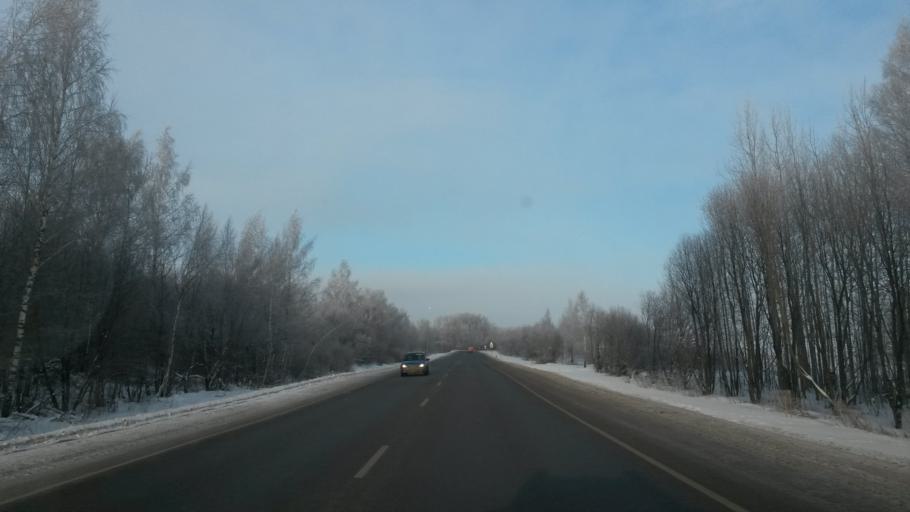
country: RU
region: Vladimir
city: Bogolyubovo
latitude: 56.2083
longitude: 40.4421
